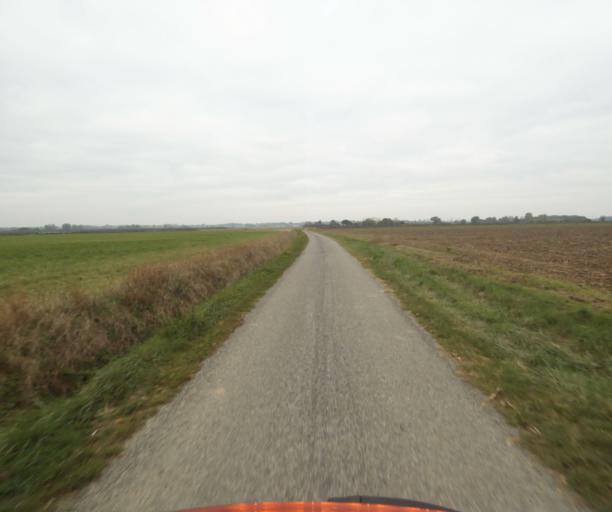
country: FR
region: Midi-Pyrenees
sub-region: Departement du Tarn-et-Garonne
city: Verdun-sur-Garonne
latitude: 43.8102
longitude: 1.2386
